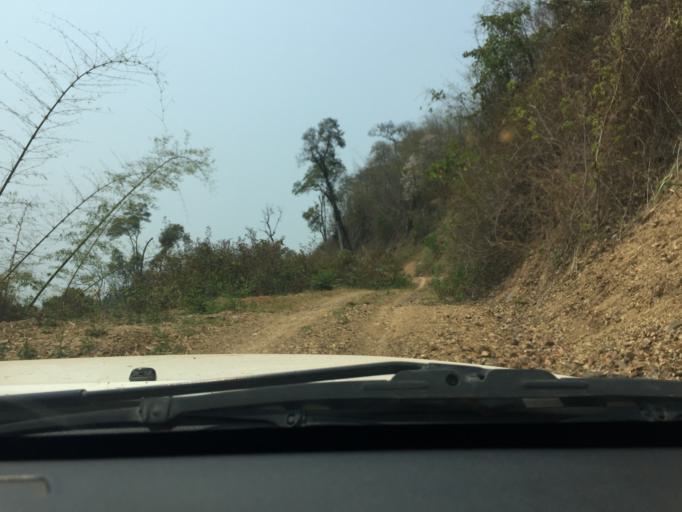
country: LA
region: Loungnamtha
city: Muang Nale
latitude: 20.6188
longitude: 101.6101
